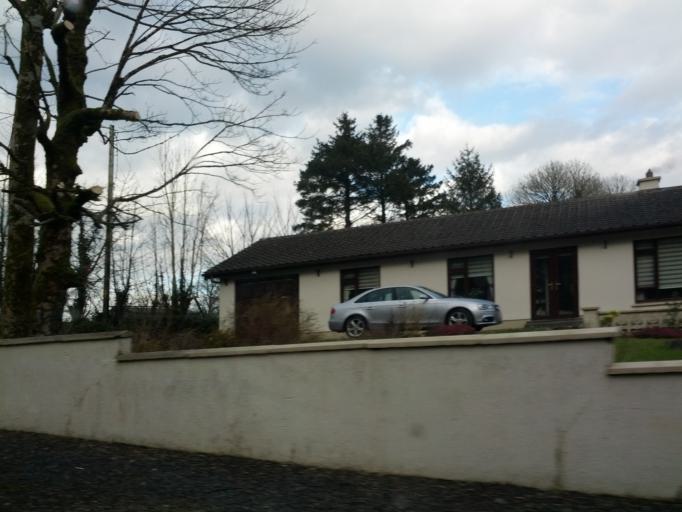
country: IE
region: Connaught
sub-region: County Galway
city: Athenry
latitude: 53.4093
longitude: -8.5849
